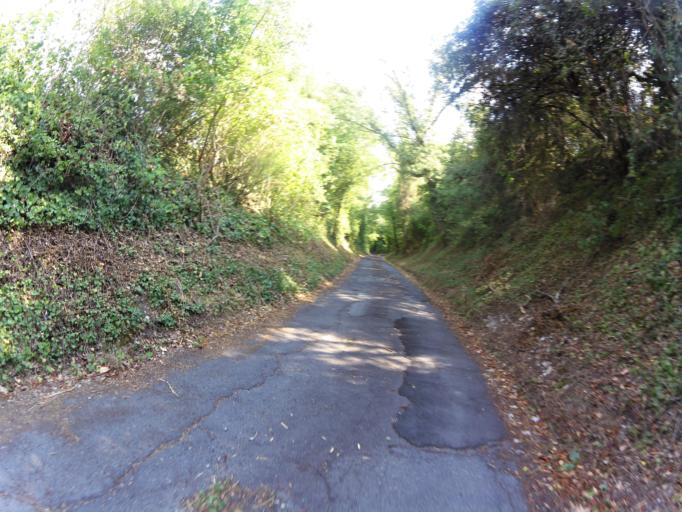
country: DE
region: Bavaria
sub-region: Regierungsbezirk Unterfranken
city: Ochsenfurt
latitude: 49.6615
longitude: 10.0611
